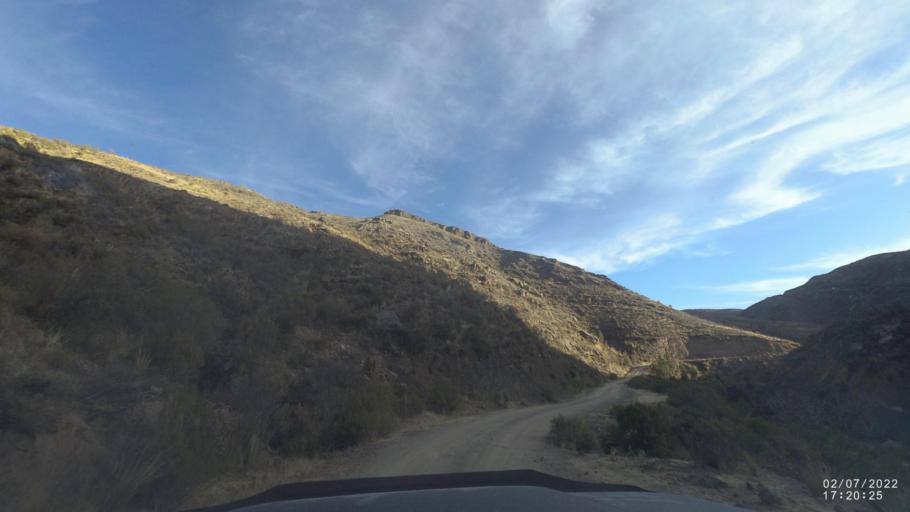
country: BO
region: Cochabamba
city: Irpa Irpa
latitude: -17.8774
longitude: -66.5949
